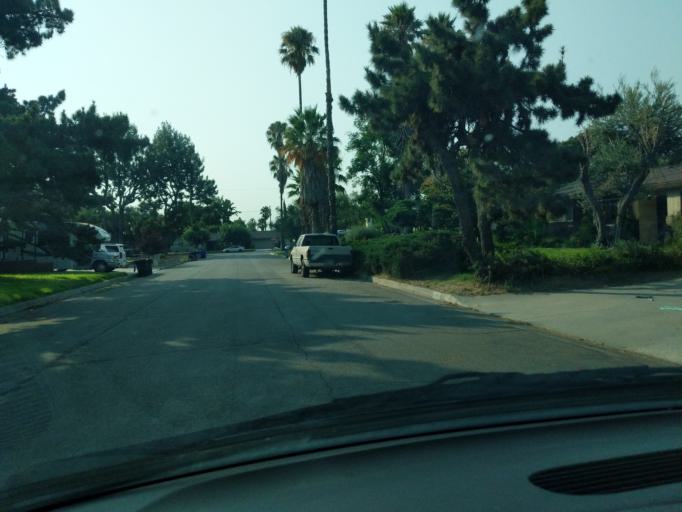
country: US
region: California
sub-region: San Bernardino County
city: Muscoy
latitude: 34.1470
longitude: -117.3825
